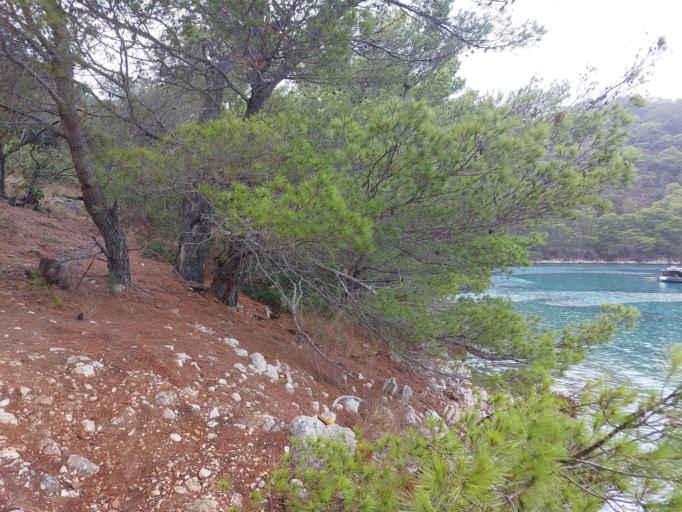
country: HR
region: Dubrovacko-Neretvanska
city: Smokvica
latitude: 42.7569
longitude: 16.8102
